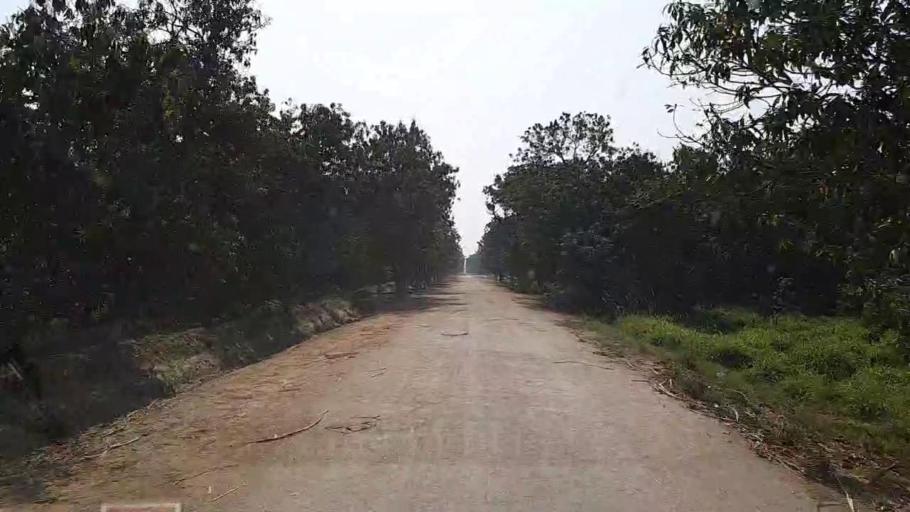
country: PK
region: Sindh
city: Mirwah Gorchani
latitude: 25.3260
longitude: 69.0075
